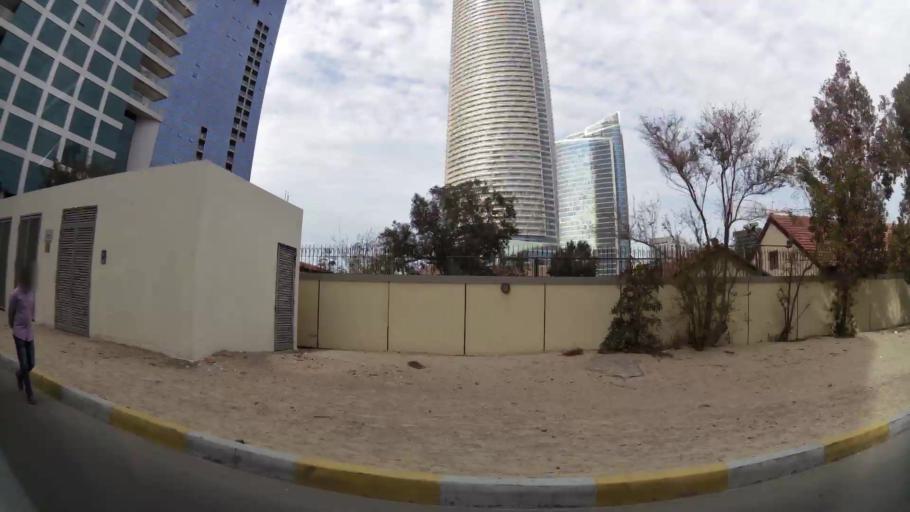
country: AE
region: Abu Dhabi
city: Abu Dhabi
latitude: 24.4825
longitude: 54.3509
